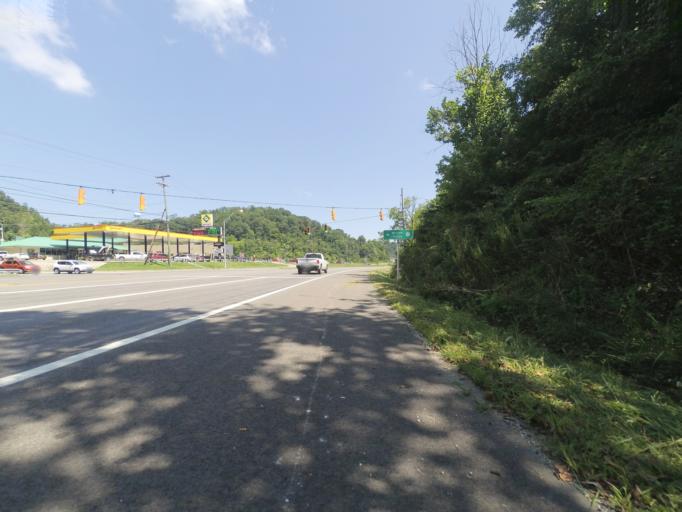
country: US
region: West Virginia
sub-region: Cabell County
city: Huntington
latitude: 38.3870
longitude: -82.4568
